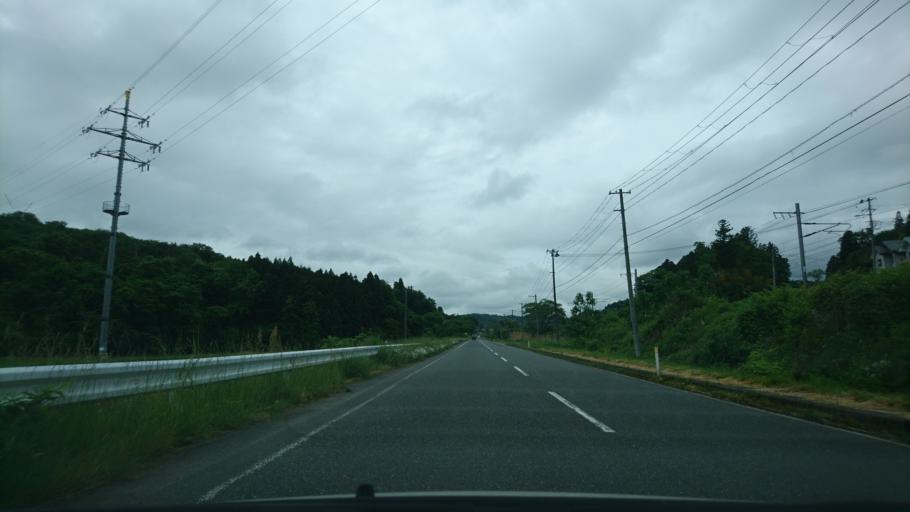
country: JP
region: Iwate
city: Ichinoseki
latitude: 38.8978
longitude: 141.1279
